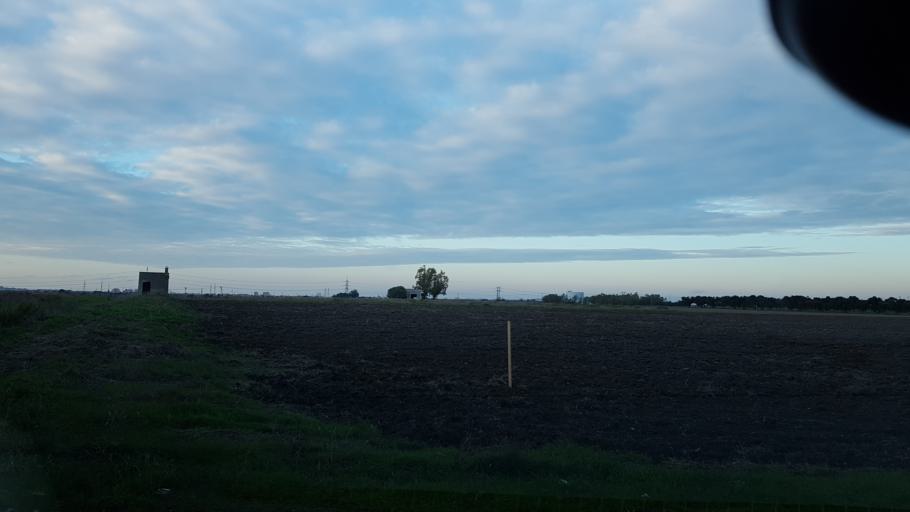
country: IT
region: Apulia
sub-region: Provincia di Brindisi
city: La Rosa
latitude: 40.5947
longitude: 17.9836
